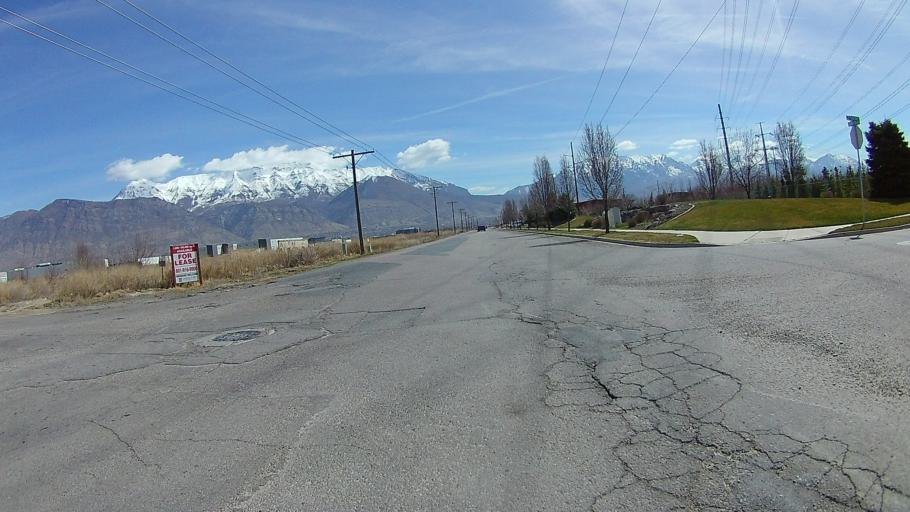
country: US
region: Utah
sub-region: Utah County
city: American Fork
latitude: 40.3476
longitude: -111.7859
